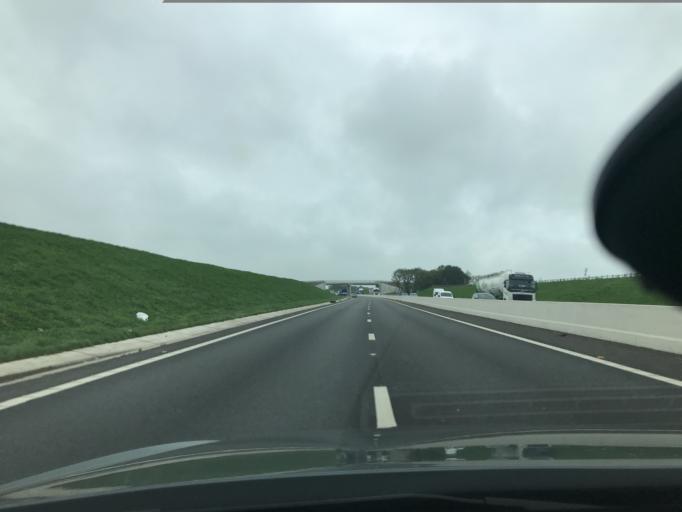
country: GB
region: England
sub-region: Cheshire East
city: Mere
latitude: 53.3501
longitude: -2.4077
